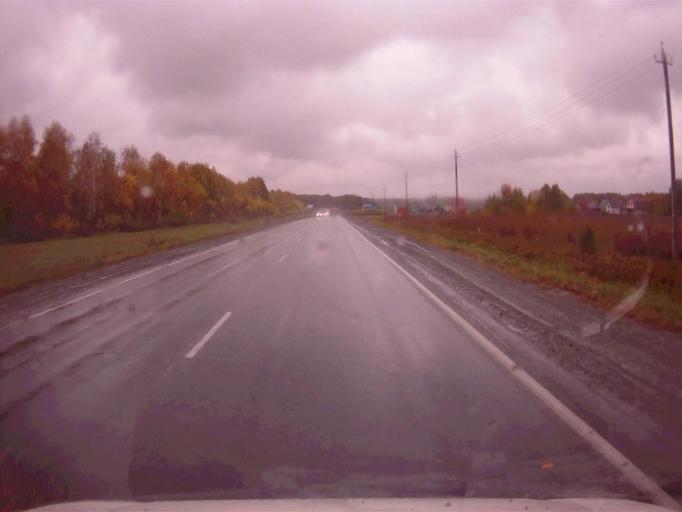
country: RU
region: Chelyabinsk
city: Argayash
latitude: 55.4058
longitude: 61.0600
